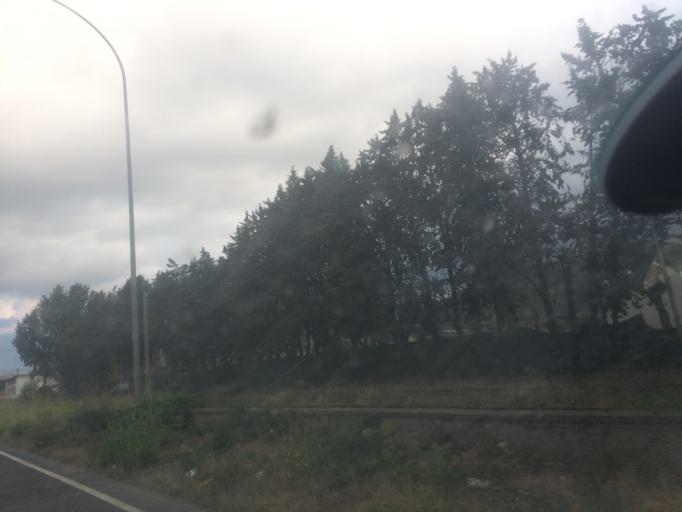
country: IT
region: Tuscany
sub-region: Provincia di Massa-Carrara
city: Carrara
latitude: 44.0372
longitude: 10.0851
